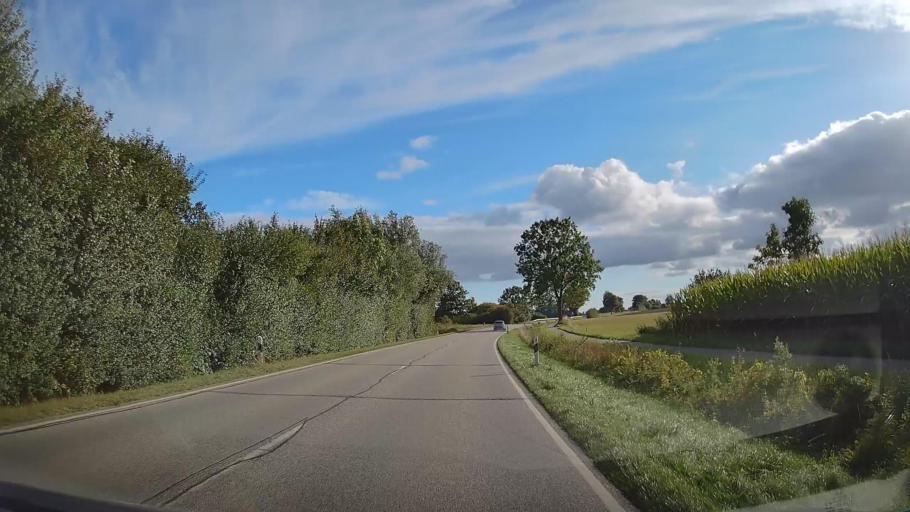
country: DE
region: Schleswig-Holstein
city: Rabel
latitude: 54.7205
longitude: 9.9541
